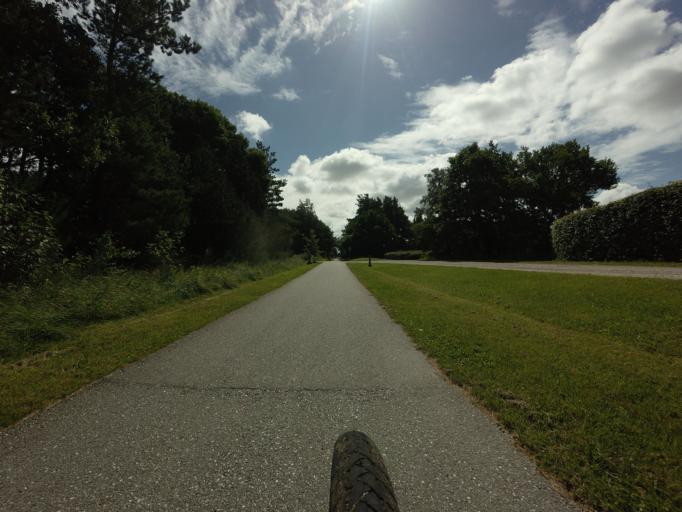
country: DK
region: Central Jutland
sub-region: Norddjurs Kommune
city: Auning
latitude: 56.4343
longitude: 10.3735
